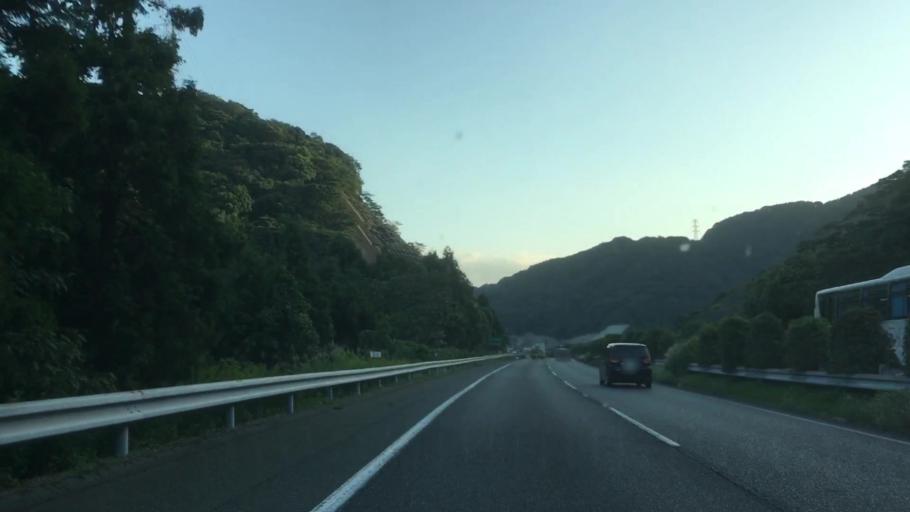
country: JP
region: Yamaguchi
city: Shimonoseki
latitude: 33.8931
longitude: 130.9716
